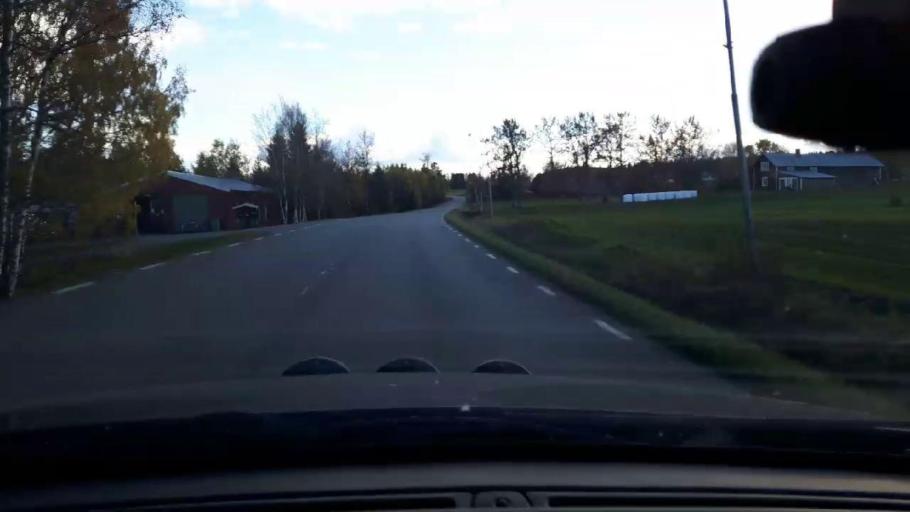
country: SE
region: Jaemtland
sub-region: Bergs Kommun
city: Hoverberg
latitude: 63.0256
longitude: 14.3445
